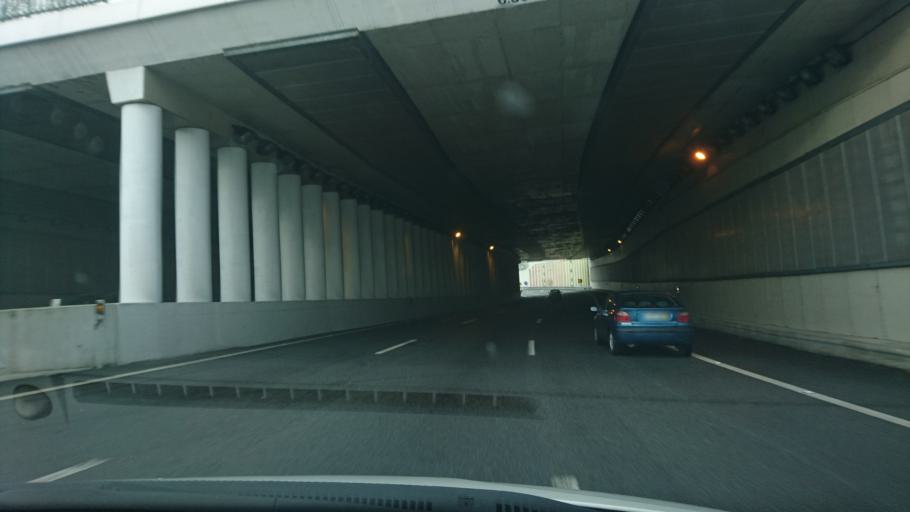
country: PT
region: Porto
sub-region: Gondomar
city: Rio Tinto
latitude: 41.1583
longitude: -8.5666
